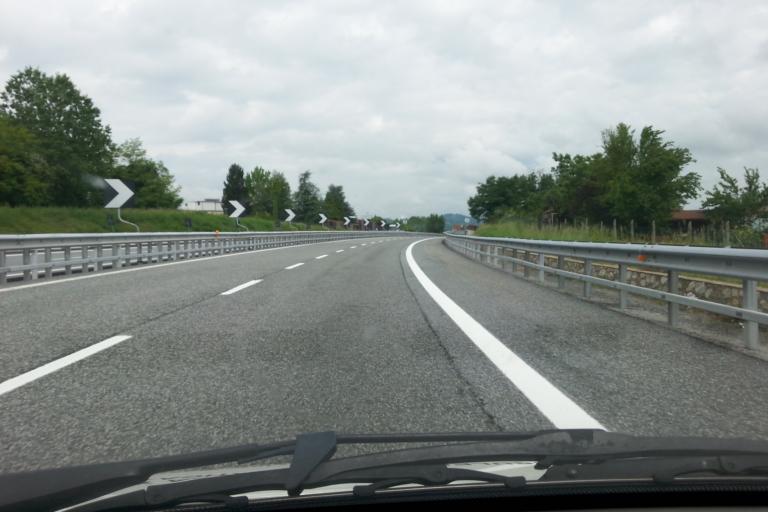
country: IT
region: Piedmont
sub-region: Provincia di Cuneo
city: Lesegno
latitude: 44.3982
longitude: 7.9770
